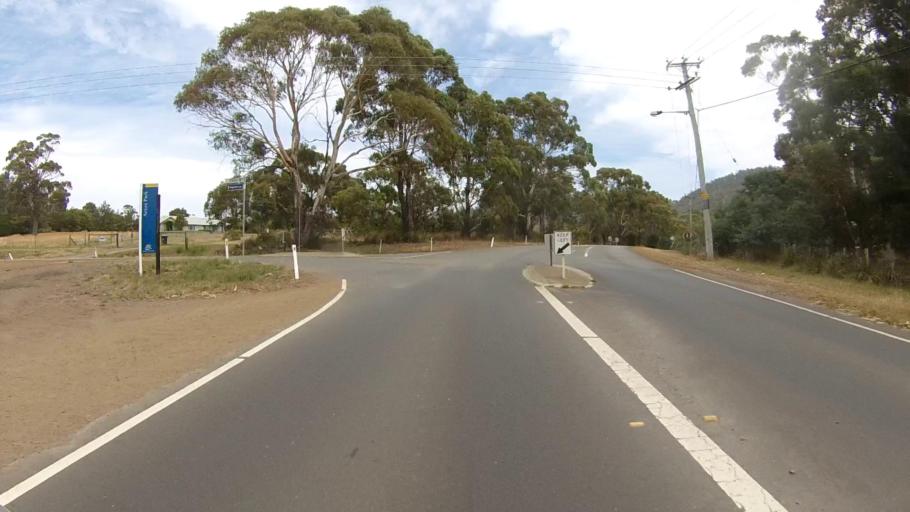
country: AU
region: Tasmania
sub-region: Clarence
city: Acton Park
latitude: -42.8676
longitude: 147.4870
